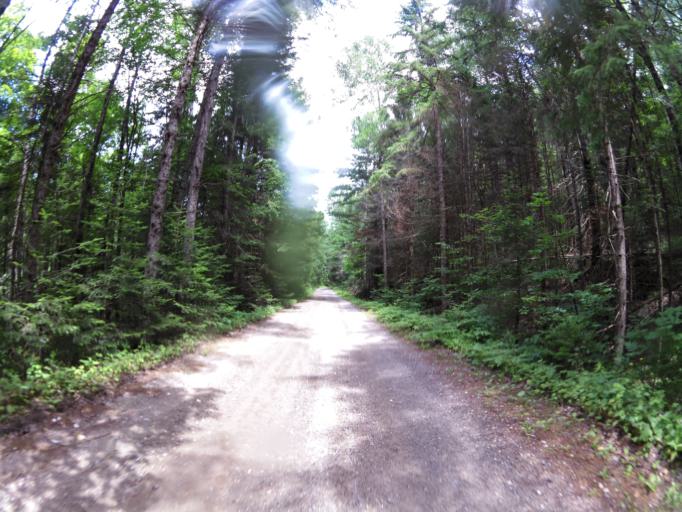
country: CA
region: Ontario
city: Renfrew
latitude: 45.0937
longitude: -76.7152
